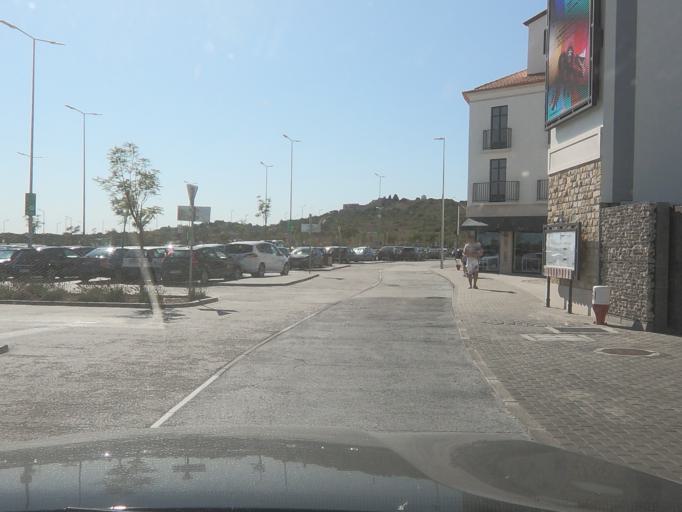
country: PT
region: Faro
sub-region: Loule
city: Almancil
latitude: 37.0989
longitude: -8.0000
